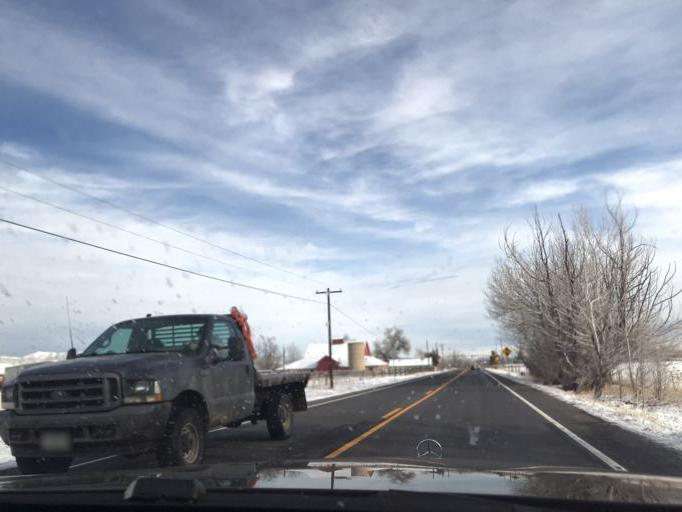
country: US
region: Colorado
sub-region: Boulder County
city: Superior
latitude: 39.9834
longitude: -105.2128
